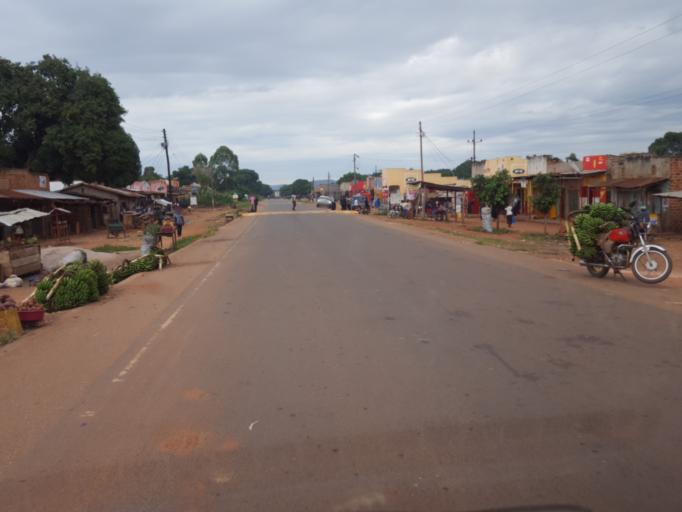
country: UG
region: Central Region
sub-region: Kiboga District
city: Kiboga
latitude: 1.0298
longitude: 31.6793
